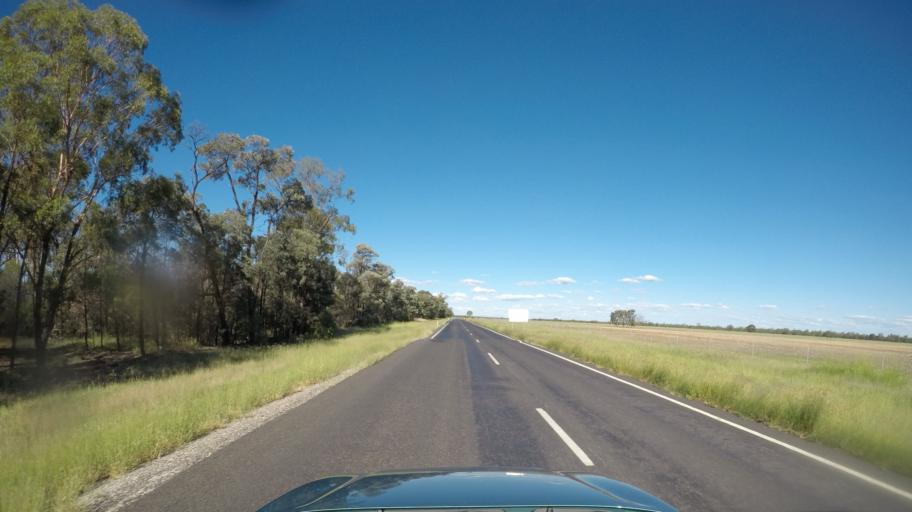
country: AU
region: Queensland
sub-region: Goondiwindi
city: Goondiwindi
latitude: -28.1557
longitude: 150.6703
